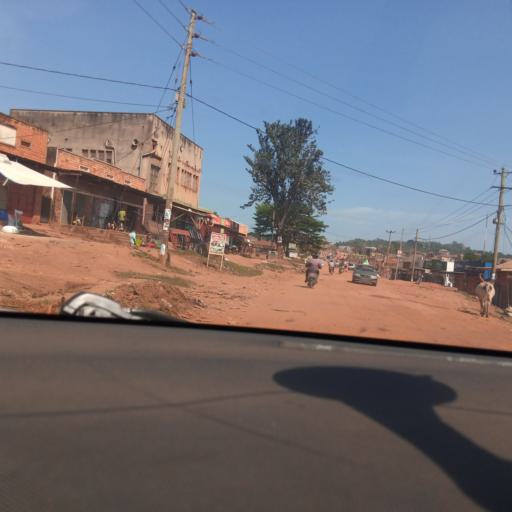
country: UG
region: Central Region
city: Masaka
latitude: -0.3138
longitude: 31.7582
